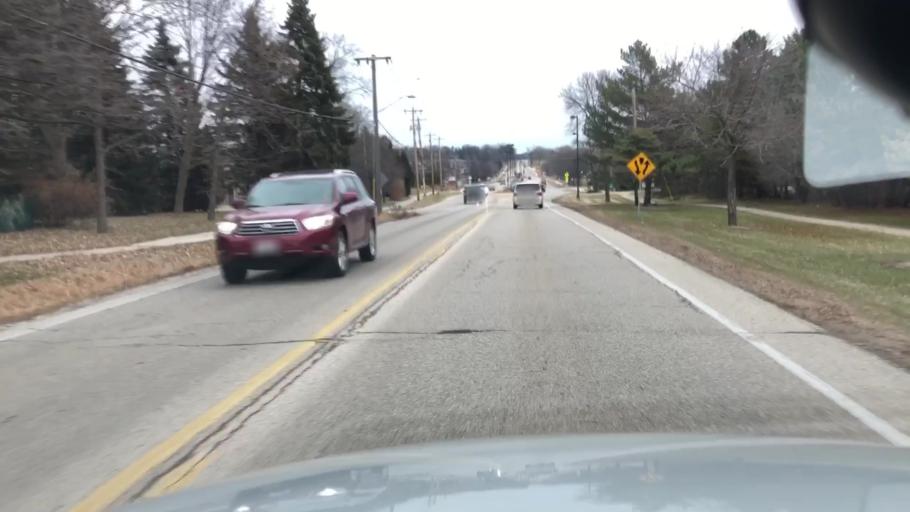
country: US
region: Wisconsin
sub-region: Waukesha County
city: Brookfield
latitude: 43.0611
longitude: -88.1326
